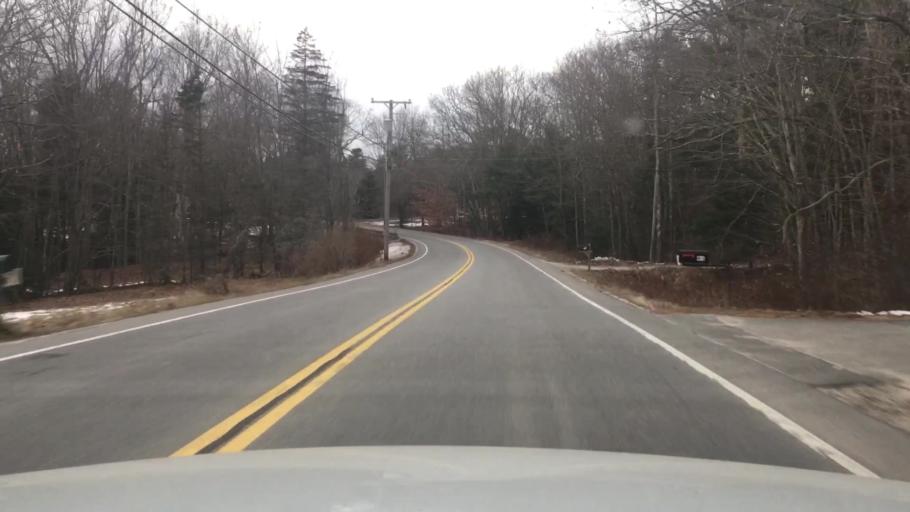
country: US
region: Maine
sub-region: Cumberland County
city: Freeport
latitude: 43.8581
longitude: -70.0714
